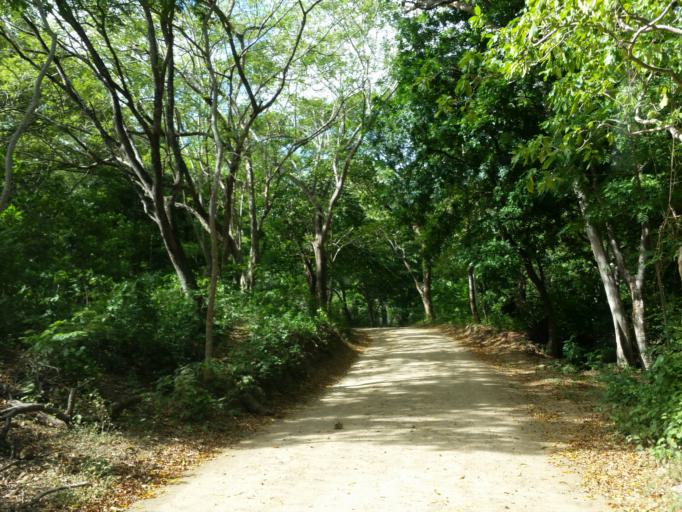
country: NI
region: Rivas
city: San Juan del Sur
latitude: 11.2250
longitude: -85.8271
